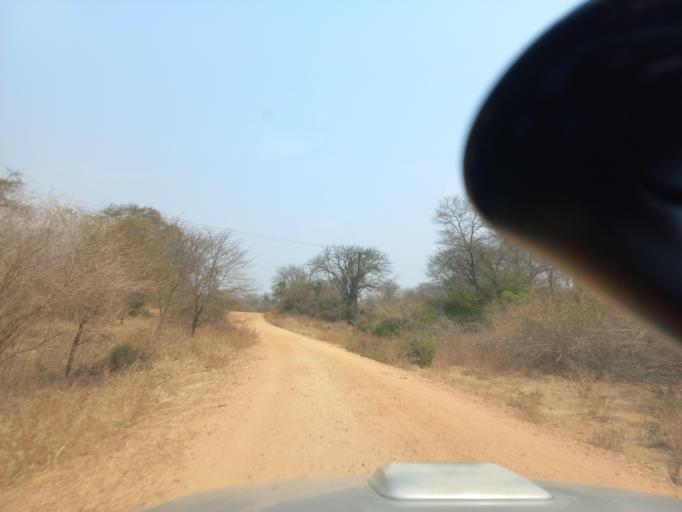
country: ZW
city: Chirundu
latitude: -15.9428
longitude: 28.8202
